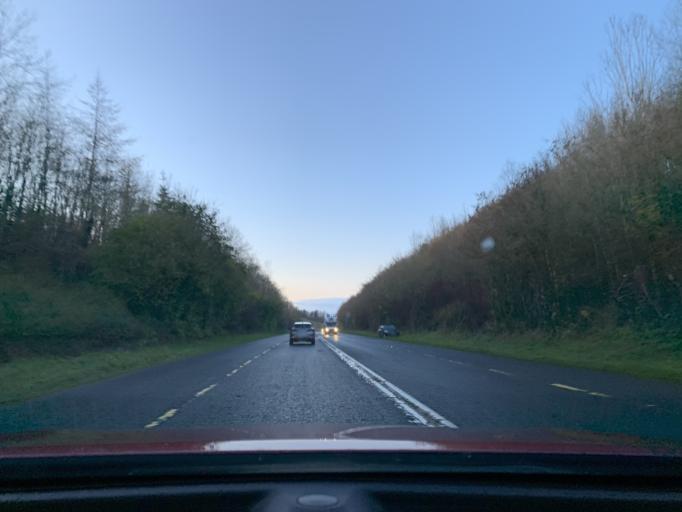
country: IE
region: Connaught
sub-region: County Leitrim
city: Carrick-on-Shannon
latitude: 53.9212
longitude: -7.9895
